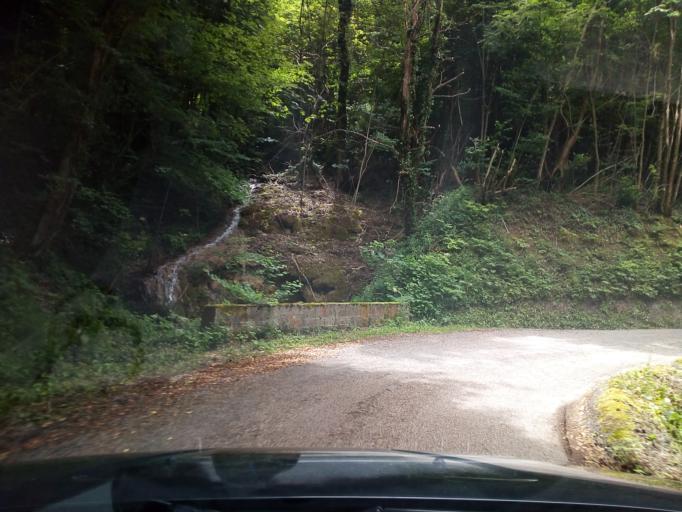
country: FR
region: Rhone-Alpes
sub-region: Departement de l'Isere
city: Saint-Martin-d'Heres
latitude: 45.1606
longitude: 5.7841
